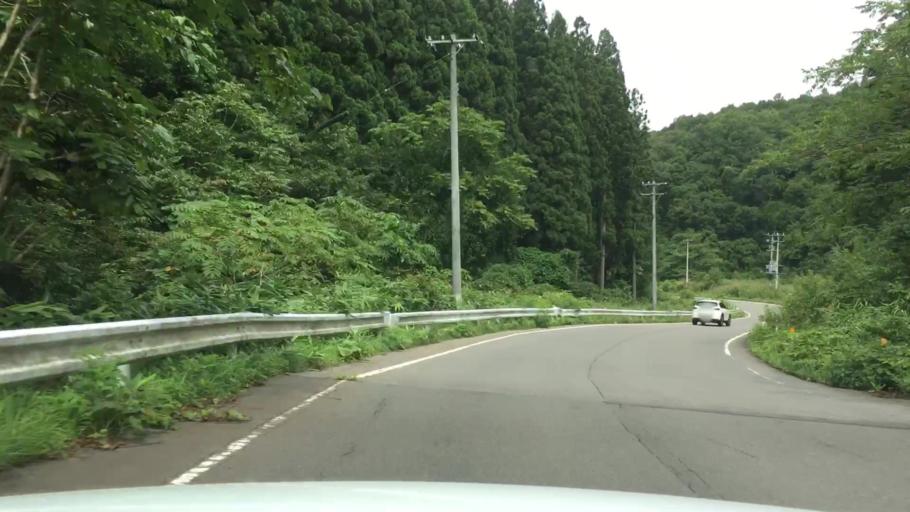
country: JP
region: Aomori
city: Shimokizukuri
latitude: 40.7302
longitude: 140.2519
